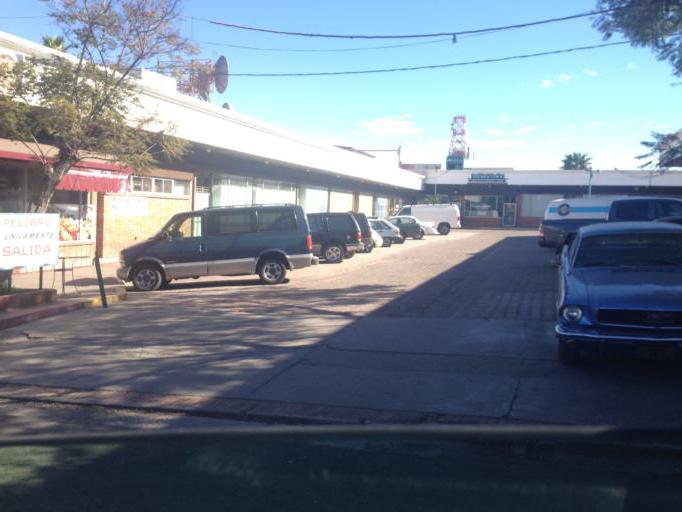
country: MX
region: Baja California
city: Tijuana
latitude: 32.5234
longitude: -117.0323
